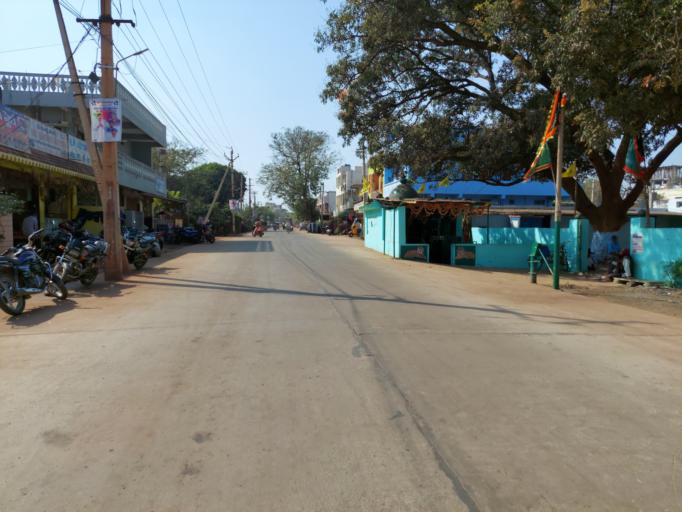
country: IN
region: Telangana
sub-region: Rangareddi
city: Vikarabad
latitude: 17.3378
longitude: 77.9008
